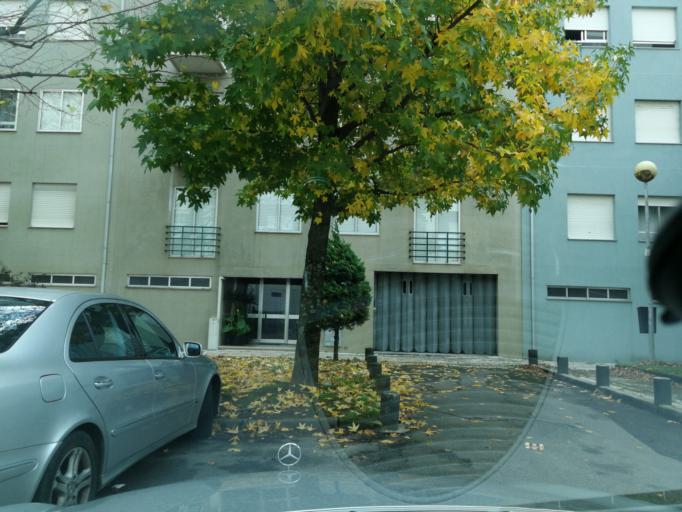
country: PT
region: Braga
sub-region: Braga
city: Braga
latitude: 41.5490
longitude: -8.4091
